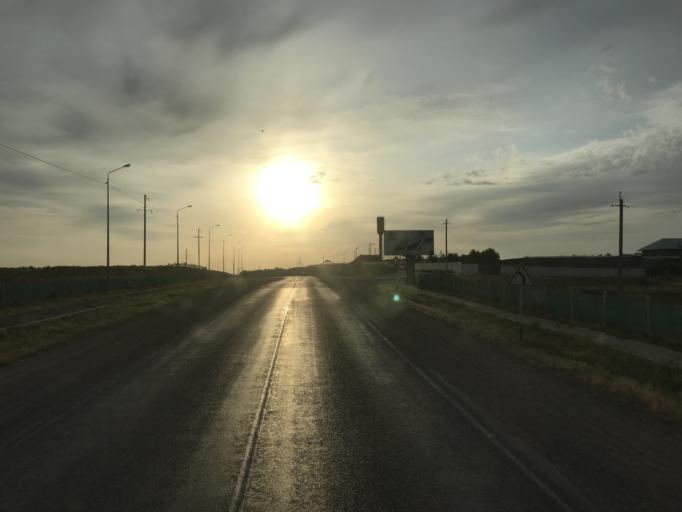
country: KZ
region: Ongtustik Qazaqstan
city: Saryaghash
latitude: 41.4067
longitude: 69.0613
